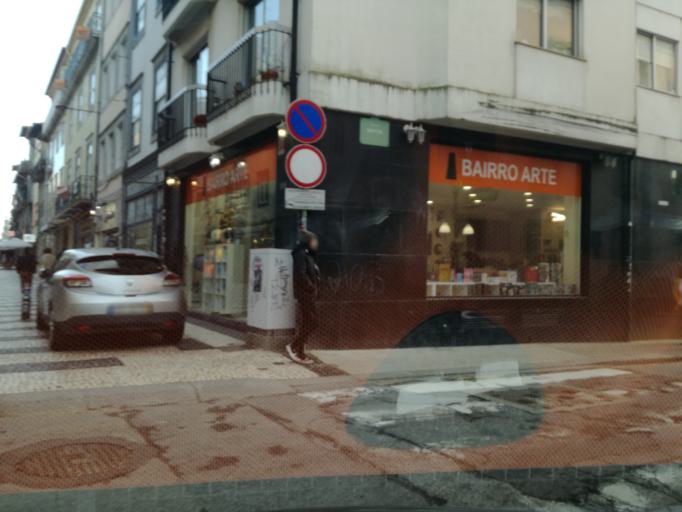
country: PT
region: Porto
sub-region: Porto
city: Porto
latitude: 41.1516
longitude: -8.6176
